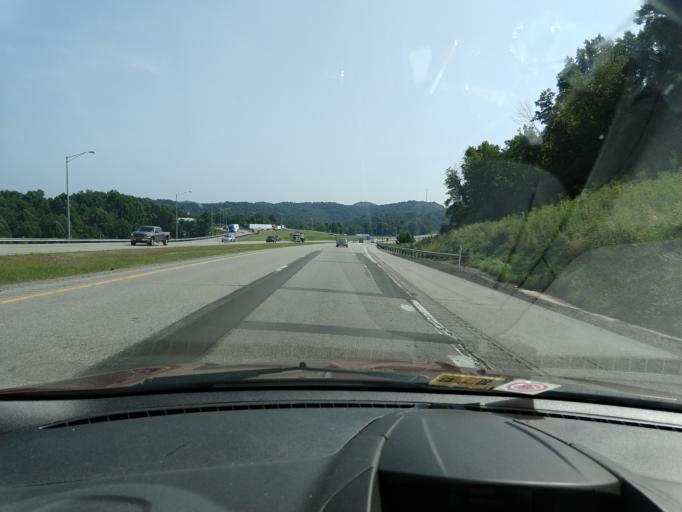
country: US
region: West Virginia
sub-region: Lewis County
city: Weston
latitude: 38.9105
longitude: -80.5985
